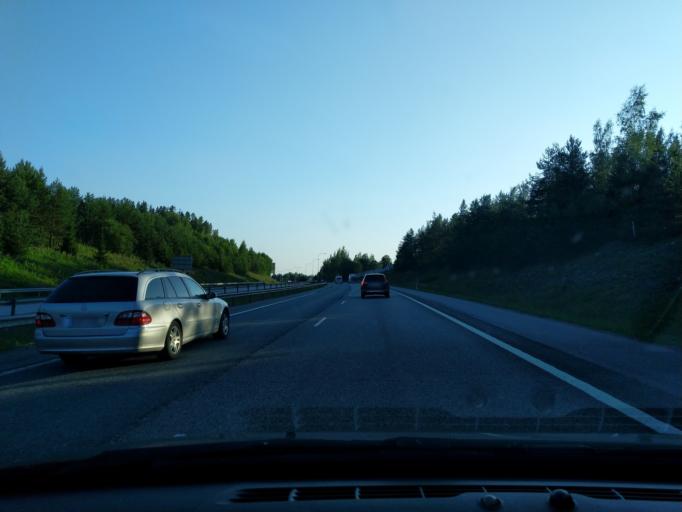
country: FI
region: Paijanne Tavastia
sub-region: Lahti
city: Lahti
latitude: 60.9390
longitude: 25.6502
